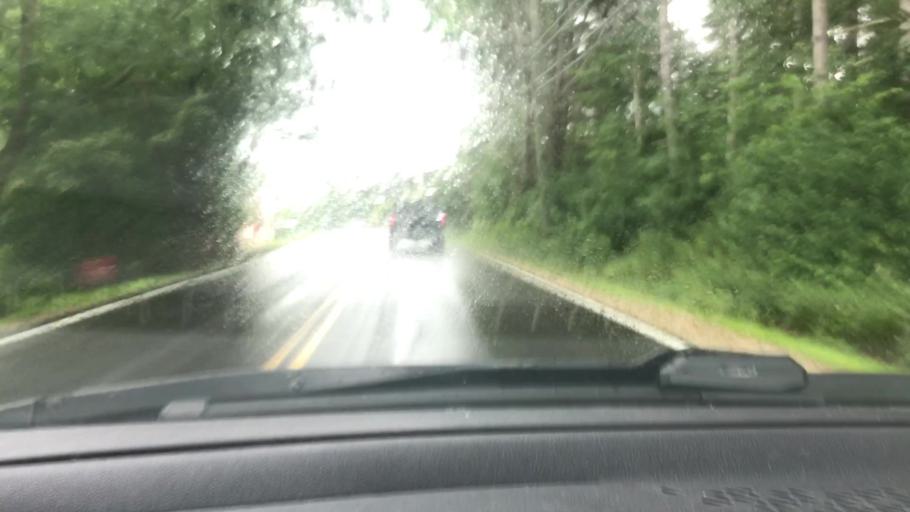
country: US
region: New Hampshire
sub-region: Merrimack County
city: Epsom
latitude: 43.1907
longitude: -71.2691
